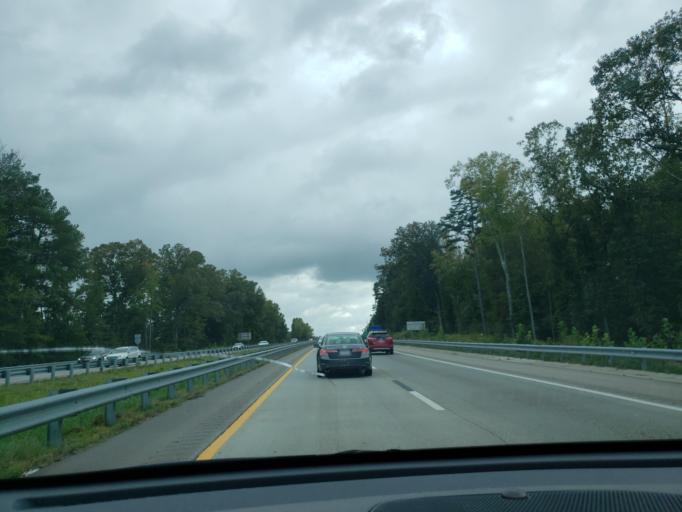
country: US
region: Virginia
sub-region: Mecklenburg County
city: Bracey
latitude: 36.5418
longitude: -78.1859
